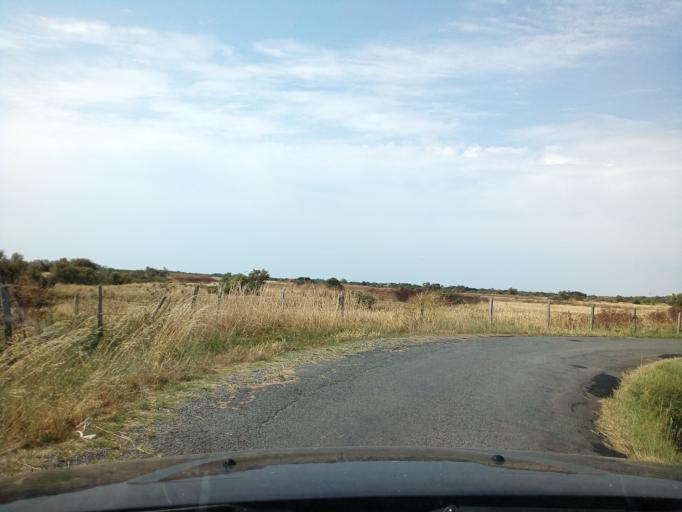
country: FR
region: Poitou-Charentes
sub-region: Departement de la Charente-Maritime
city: Dolus-d'Oleron
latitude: 45.9522
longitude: -1.2795
